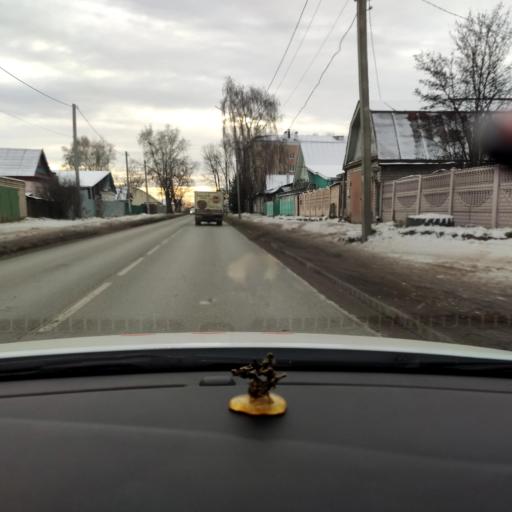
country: RU
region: Tatarstan
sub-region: Zelenodol'skiy Rayon
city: Zelenodolsk
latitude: 55.8575
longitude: 48.5326
